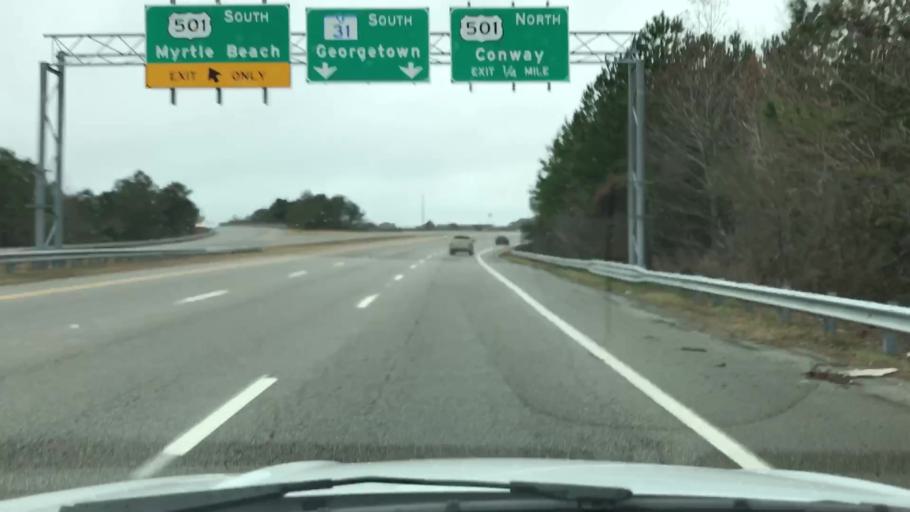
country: US
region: South Carolina
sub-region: Horry County
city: Forestbrook
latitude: 33.7414
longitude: -78.9456
